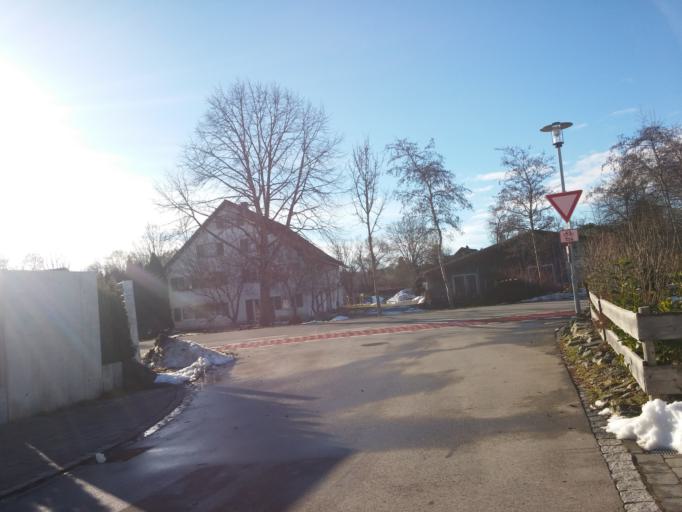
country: DE
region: Bavaria
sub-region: Swabia
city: Legau
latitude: 47.8285
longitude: 10.0981
